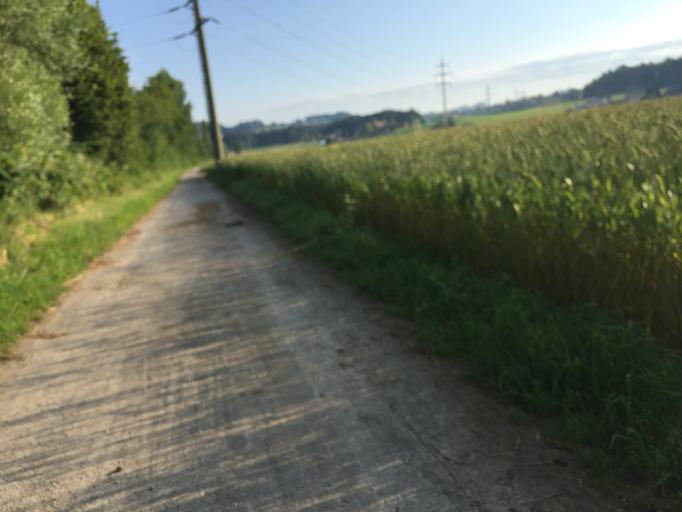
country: CH
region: Bern
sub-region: Bern-Mittelland District
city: Rubigen
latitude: 46.9137
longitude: 7.5381
